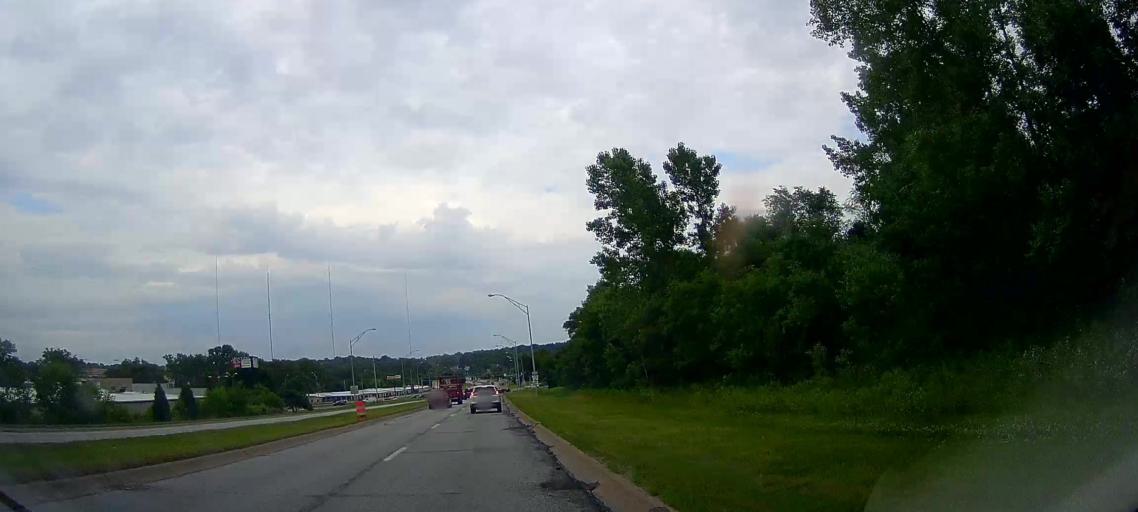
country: US
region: Nebraska
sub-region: Douglas County
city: Ralston
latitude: 41.3142
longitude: -96.0550
